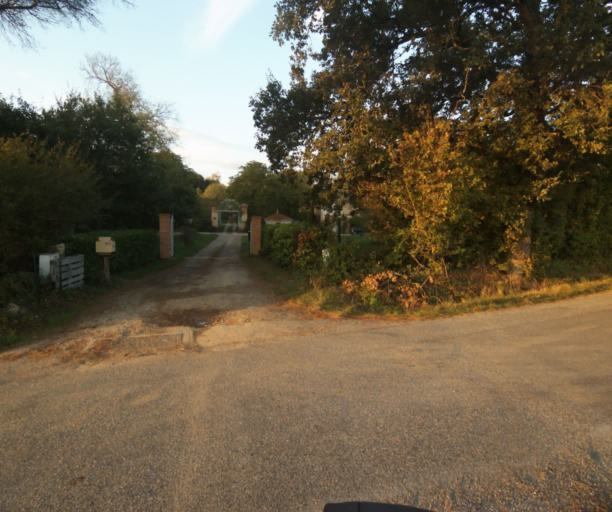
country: FR
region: Midi-Pyrenees
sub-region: Departement du Tarn-et-Garonne
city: Verdun-sur-Garonne
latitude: 43.8286
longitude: 1.1959
